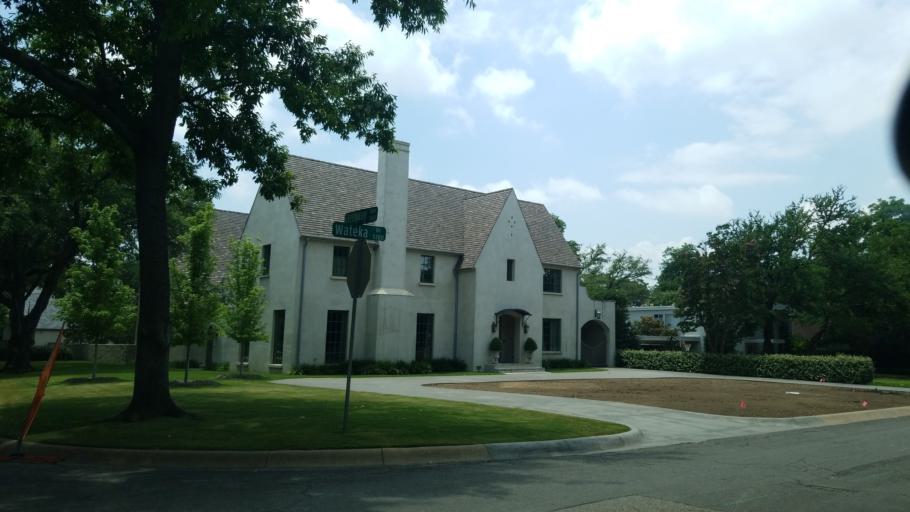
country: US
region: Texas
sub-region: Dallas County
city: University Park
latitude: 32.8439
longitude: -96.8191
